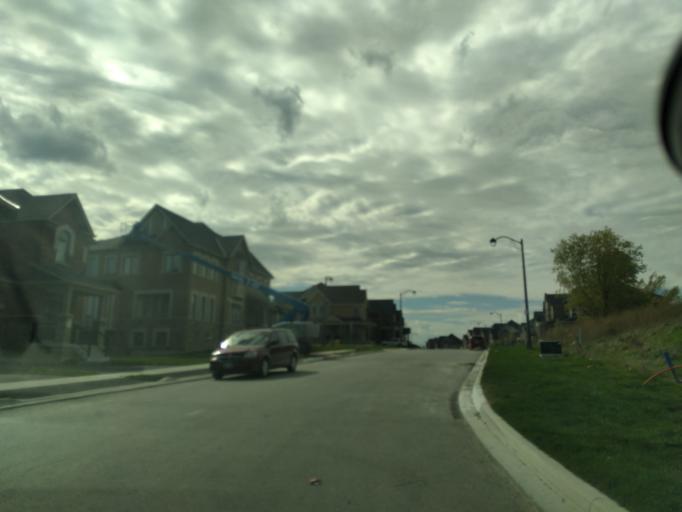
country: CA
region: Ontario
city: Newmarket
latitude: 44.0959
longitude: -79.4980
